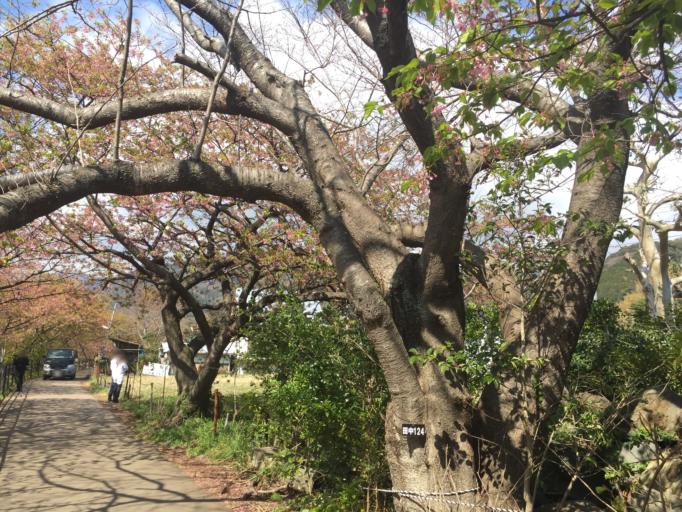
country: JP
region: Shizuoka
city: Shimoda
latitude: 34.7534
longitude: 138.9874
